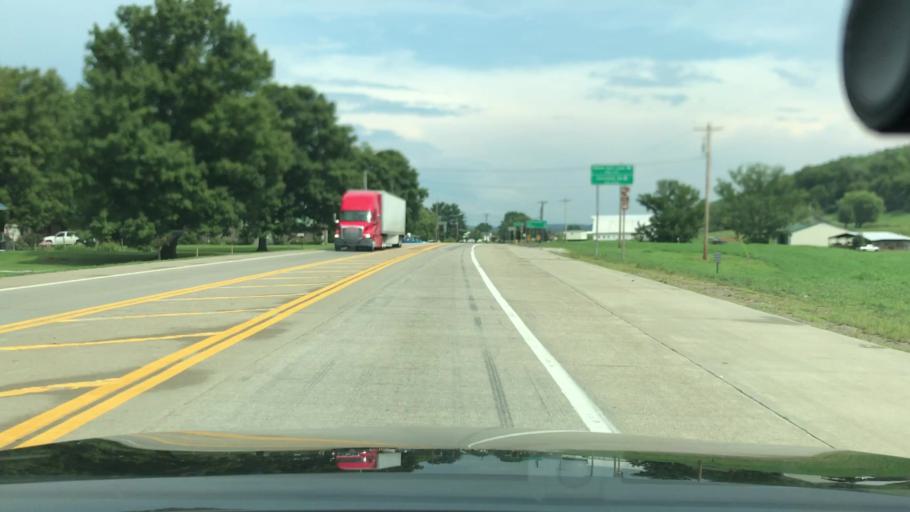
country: US
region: West Virginia
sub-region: Putnam County
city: Buffalo
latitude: 38.7658
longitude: -82.0047
